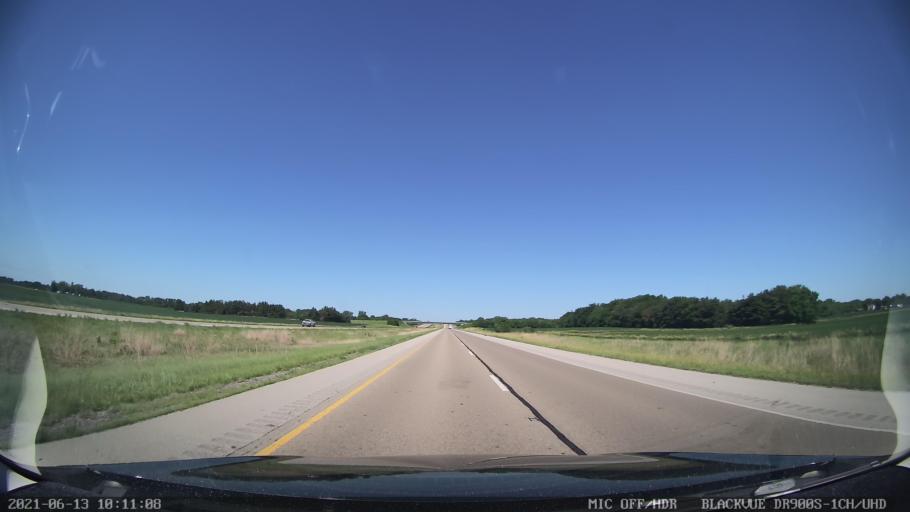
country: US
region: Illinois
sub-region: Logan County
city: Lincoln
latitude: 40.1812
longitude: -89.3524
